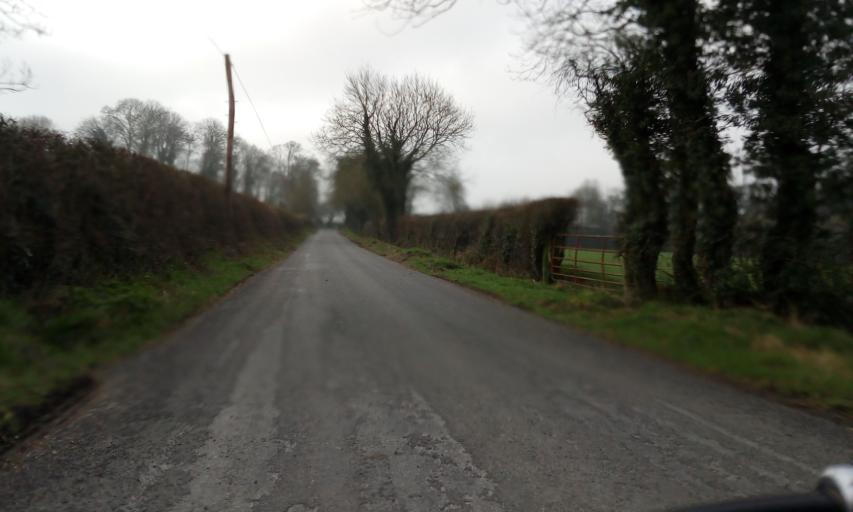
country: IE
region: Leinster
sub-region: Kilkenny
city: Kilkenny
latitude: 52.6663
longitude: -7.1862
